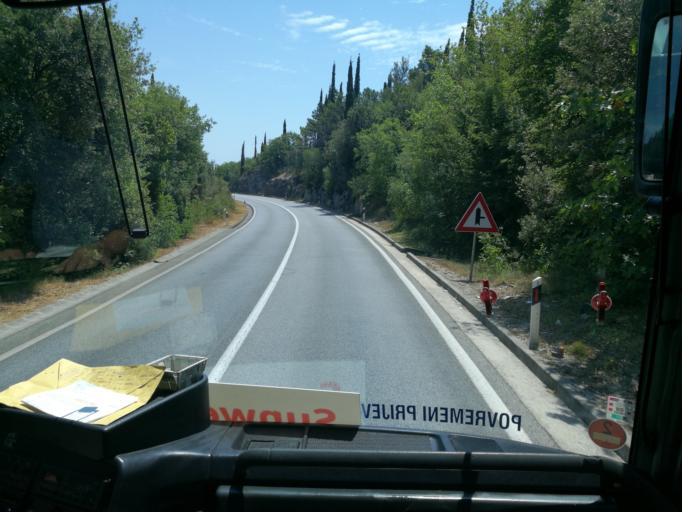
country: HR
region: Dubrovacko-Neretvanska
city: Cavtat
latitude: 42.5660
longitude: 18.2451
